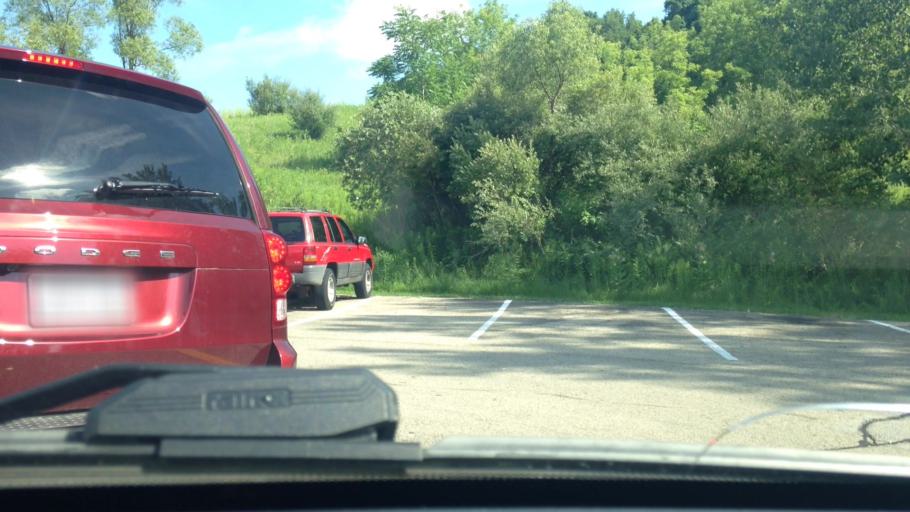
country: US
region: Wisconsin
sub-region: Dodge County
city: Mayville
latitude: 43.4933
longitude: -88.5598
